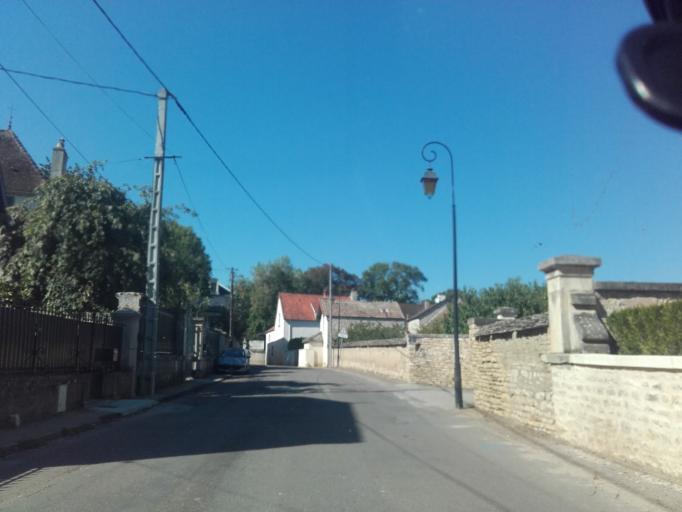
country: FR
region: Bourgogne
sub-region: Departement de la Cote-d'Or
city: Meursault
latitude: 46.9801
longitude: 4.7711
